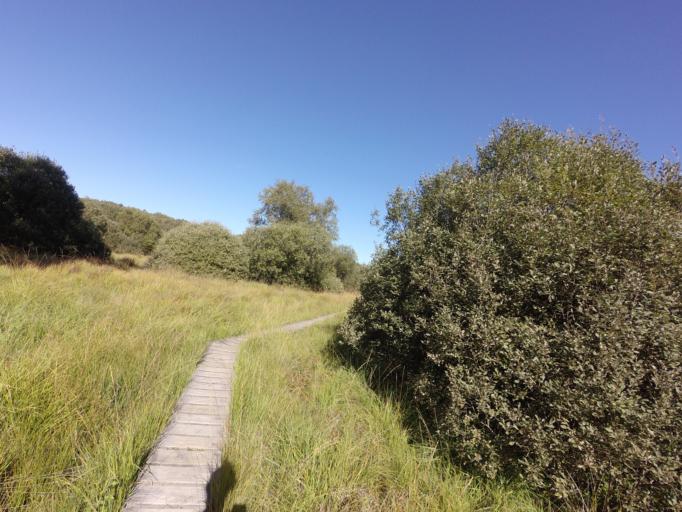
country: DE
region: North Rhine-Westphalia
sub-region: Regierungsbezirk Koln
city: Roetgen
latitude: 50.6005
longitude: 6.2087
